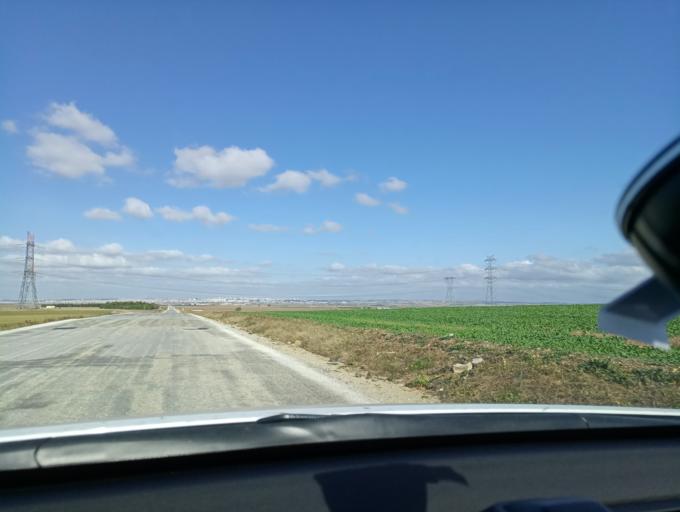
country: TR
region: Tekirdag
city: Corlu
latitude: 41.0571
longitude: 27.8348
